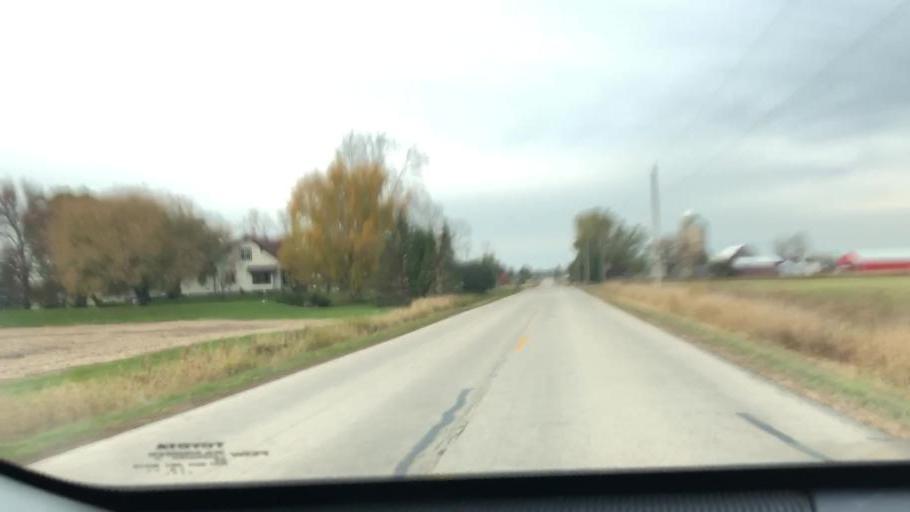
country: US
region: Wisconsin
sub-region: Outagamie County
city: Seymour
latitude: 44.4568
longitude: -88.3499
